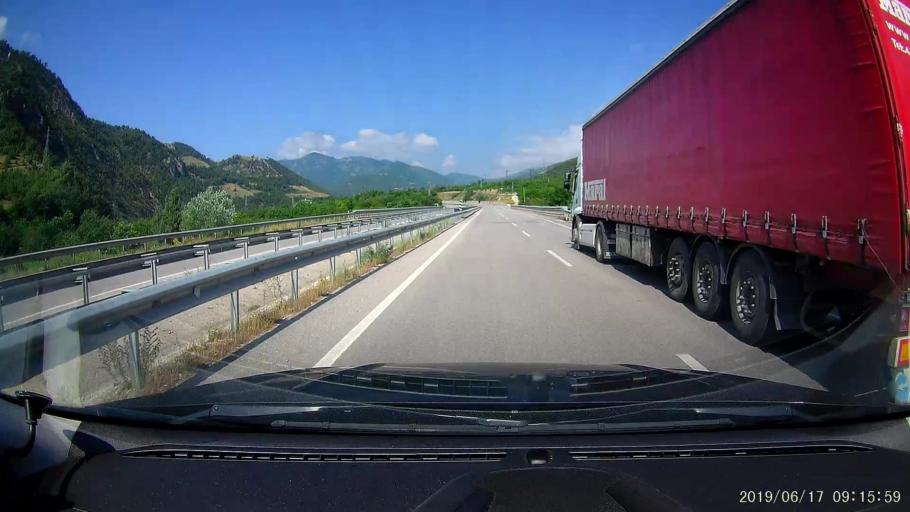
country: TR
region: Amasya
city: Akdag
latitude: 40.7463
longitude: 36.0232
